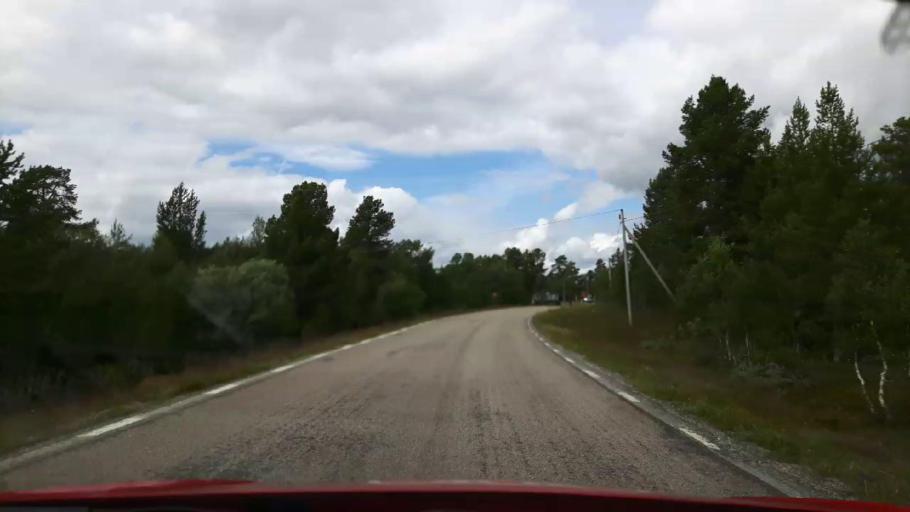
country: NO
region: Hedmark
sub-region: Engerdal
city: Engerdal
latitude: 62.2979
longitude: 12.8047
